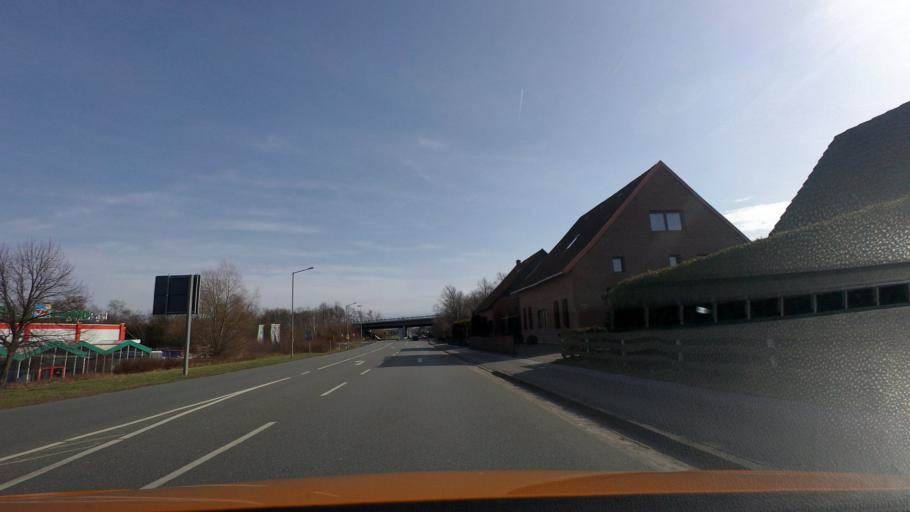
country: DE
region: Lower Saxony
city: Lauenhagen
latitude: 52.3297
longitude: 9.2328
